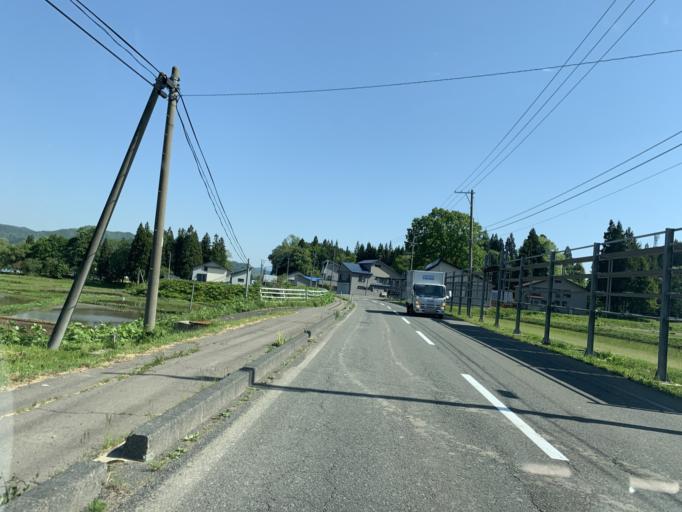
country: JP
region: Akita
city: Yokotemachi
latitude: 39.4114
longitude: 140.7492
